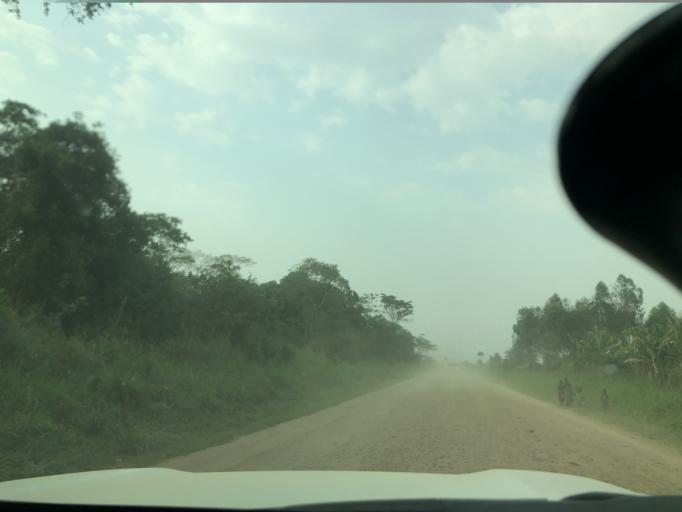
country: UG
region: Western Region
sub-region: Kasese District
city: Margherita
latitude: 0.2562
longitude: 29.6788
